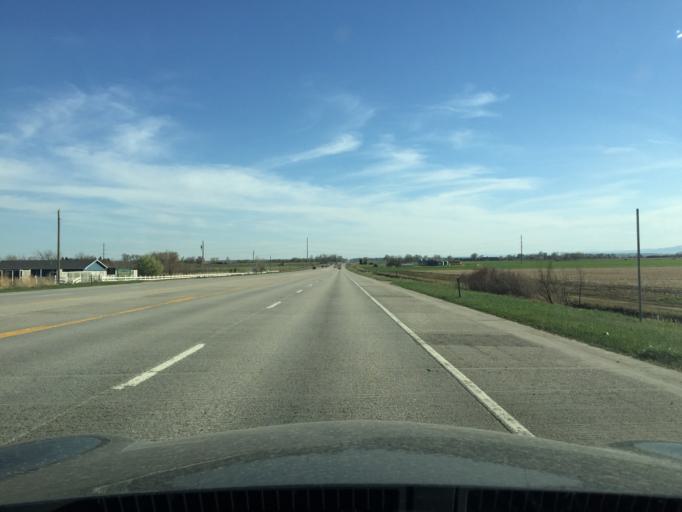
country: US
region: Colorado
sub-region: Boulder County
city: Erie
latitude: 40.0811
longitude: -105.1028
